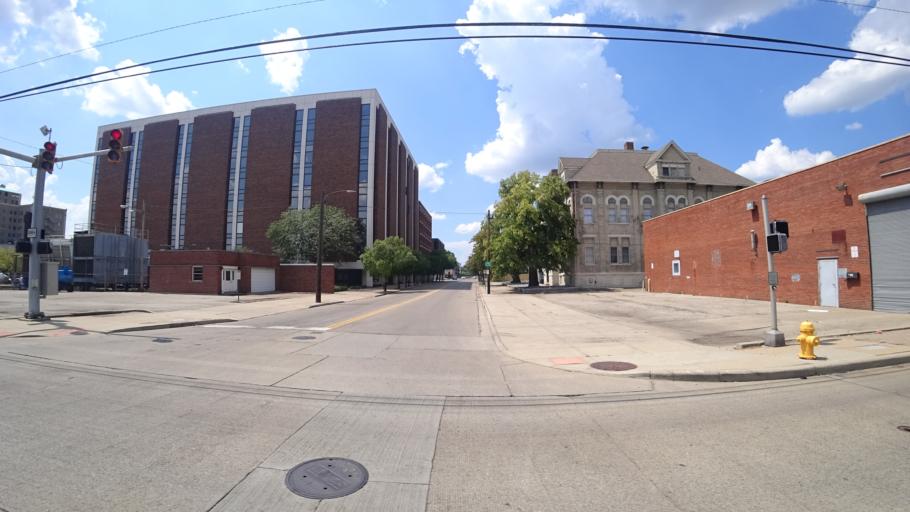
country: US
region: Ohio
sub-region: Butler County
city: Hamilton
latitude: 39.4009
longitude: -84.5578
